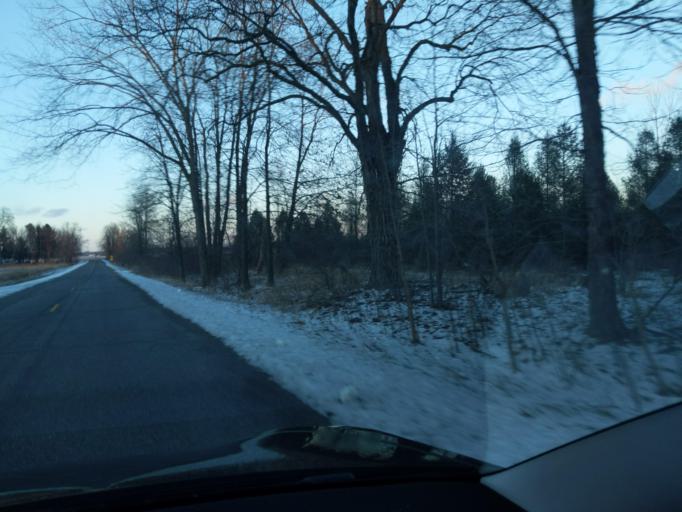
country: US
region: Michigan
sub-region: Ingham County
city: Stockbridge
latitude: 42.4647
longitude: -84.2779
